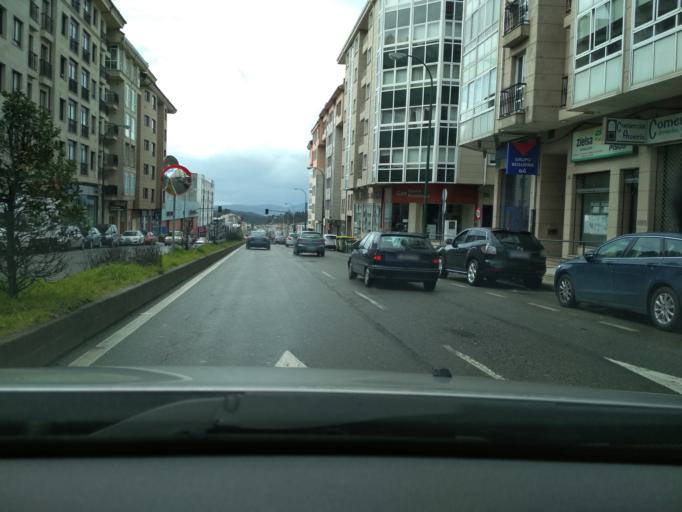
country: ES
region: Galicia
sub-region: Provincia da Coruna
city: Santiago de Compostela
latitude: 42.8414
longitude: -8.5798
